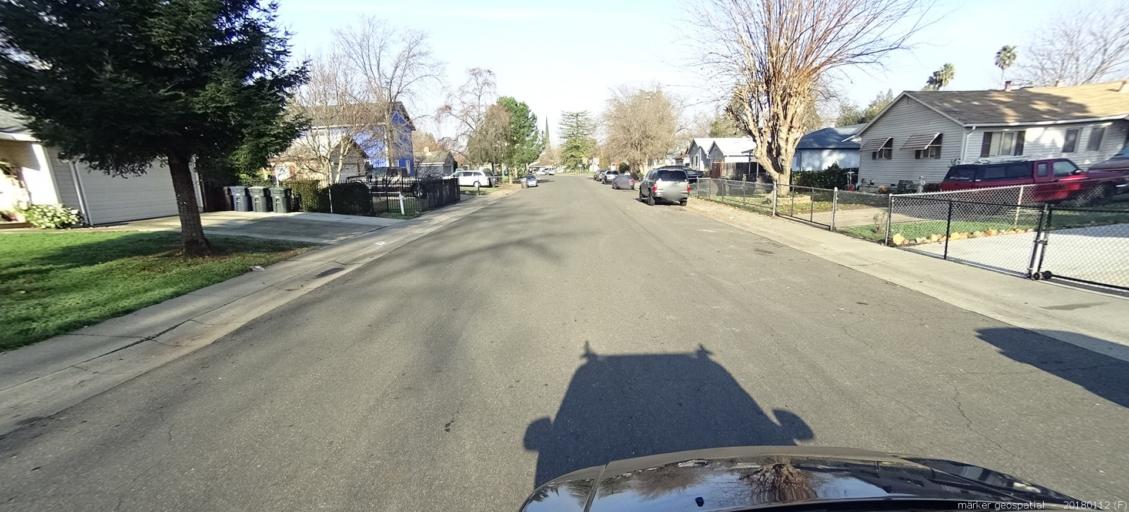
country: US
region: California
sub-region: Sacramento County
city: Rancho Cordova
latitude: 38.6125
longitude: -121.2800
